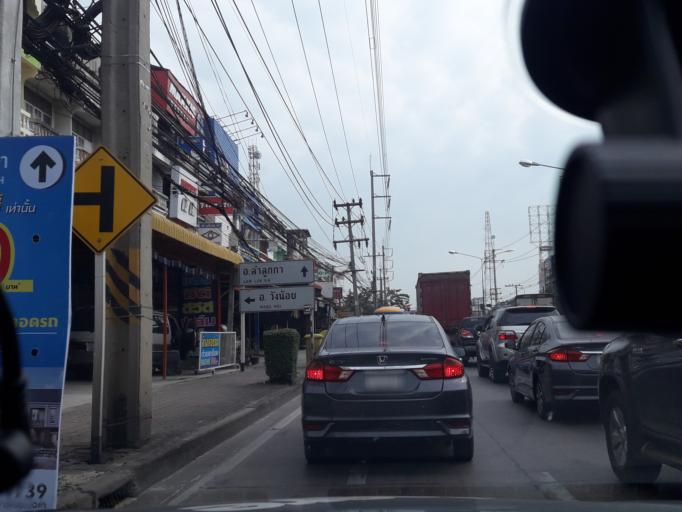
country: TH
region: Pathum Thani
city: Lam Luk Ka
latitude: 13.9349
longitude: 100.7448
